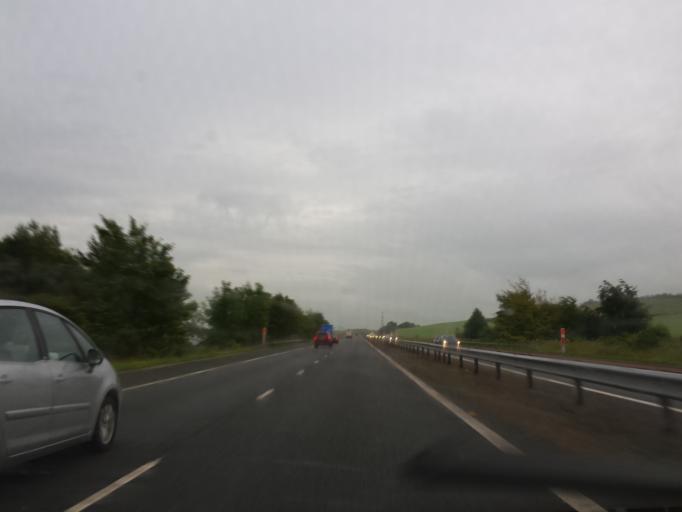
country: GB
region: Scotland
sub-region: Perth and Kinross
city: Perth
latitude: 56.3811
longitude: -3.4600
